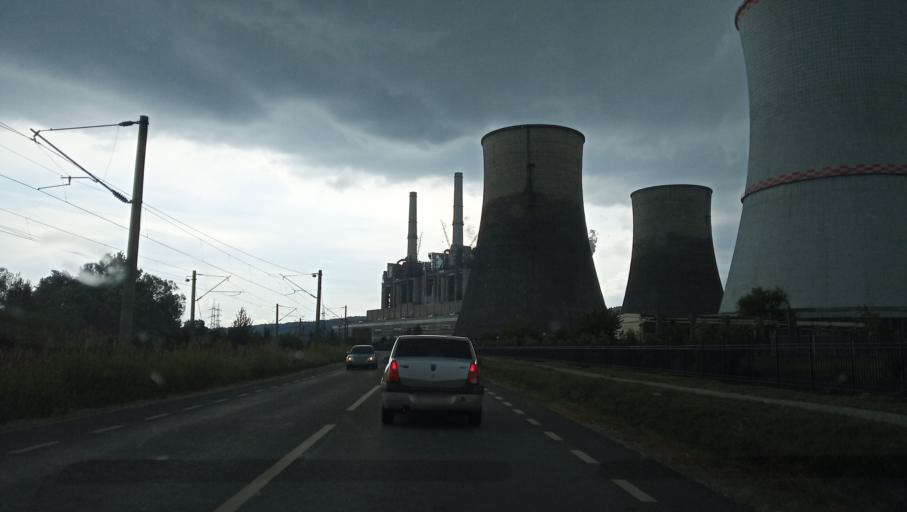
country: RO
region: Gorj
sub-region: Oras Rovinari
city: Rovinari
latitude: 44.9154
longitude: 23.1358
